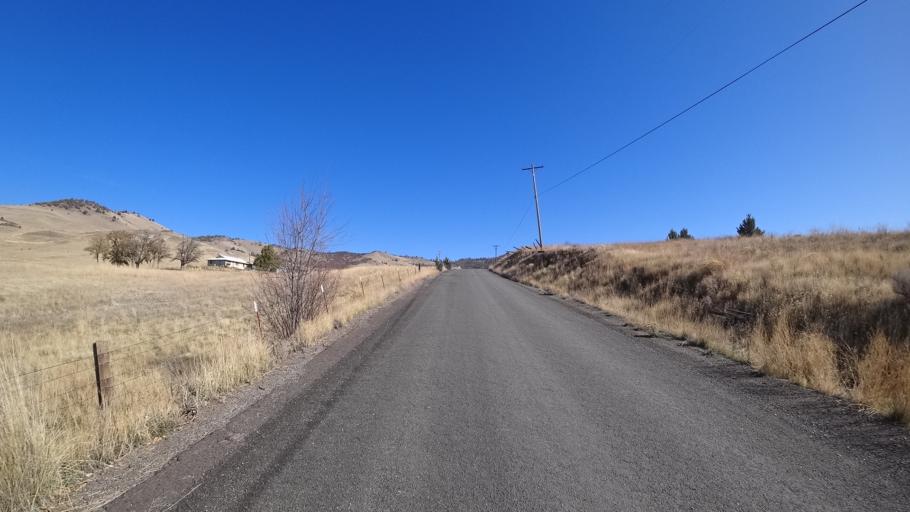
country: US
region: California
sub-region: Siskiyou County
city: Montague
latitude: 41.8301
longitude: -122.3613
